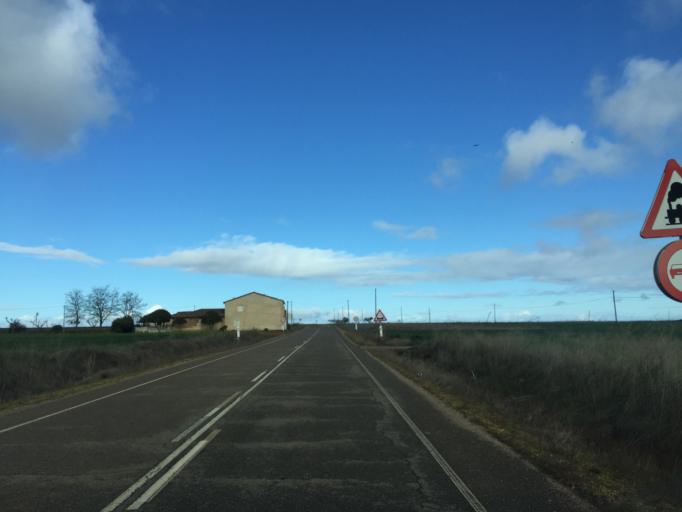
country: ES
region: Castille and Leon
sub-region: Provincia de Zamora
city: Manganeses de la Lampreana
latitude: 41.7549
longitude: -5.7177
